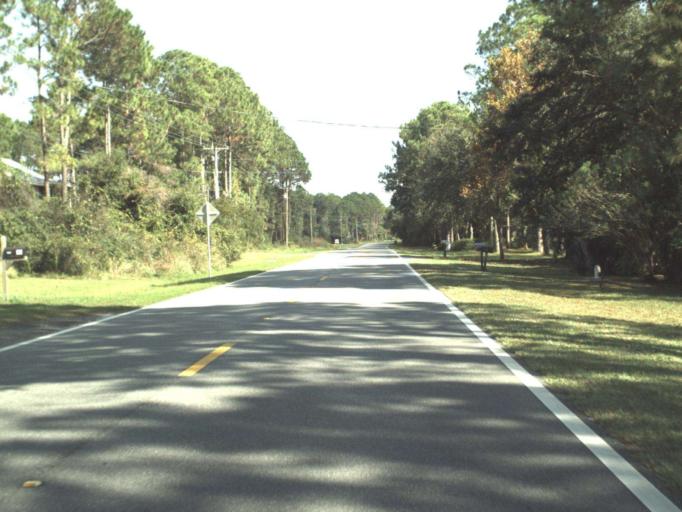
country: US
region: Florida
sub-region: Franklin County
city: Carrabelle
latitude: 29.8863
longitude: -84.5840
